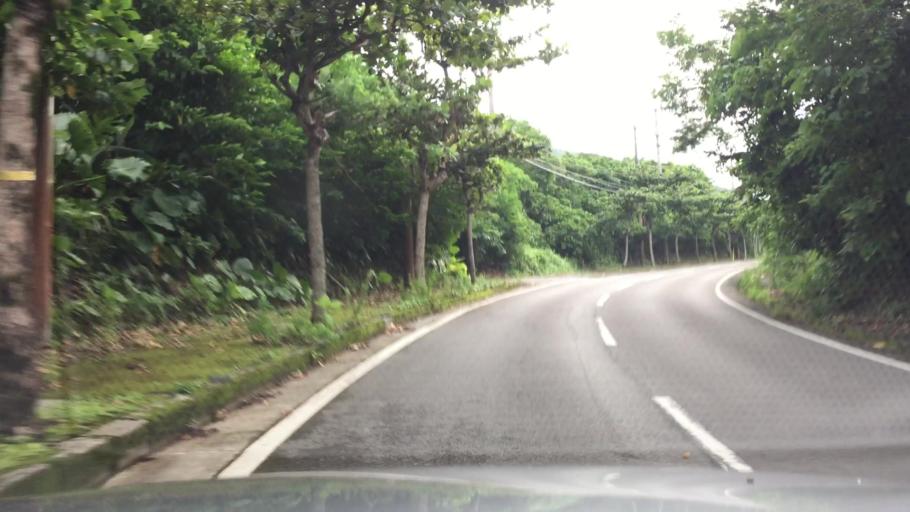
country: JP
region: Okinawa
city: Ishigaki
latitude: 24.4461
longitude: 124.1779
